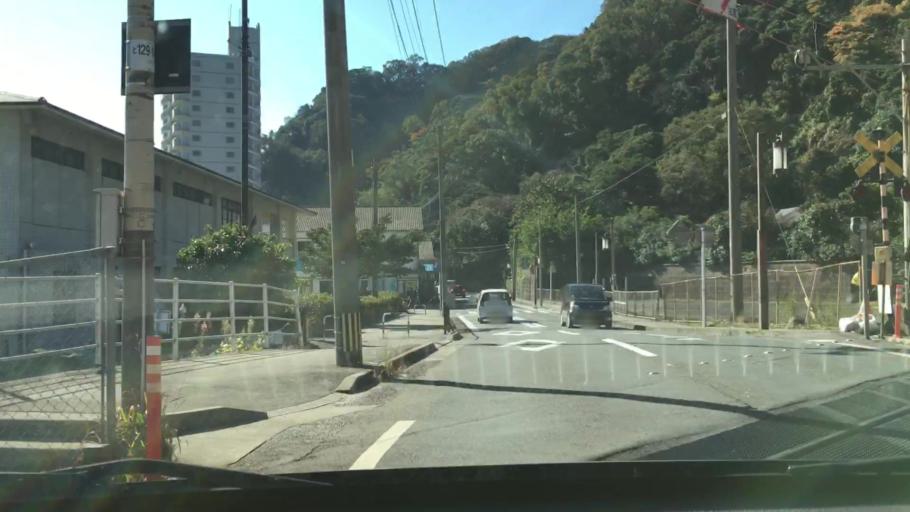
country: JP
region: Kagoshima
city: Kagoshima-shi
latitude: 31.6155
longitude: 130.5749
